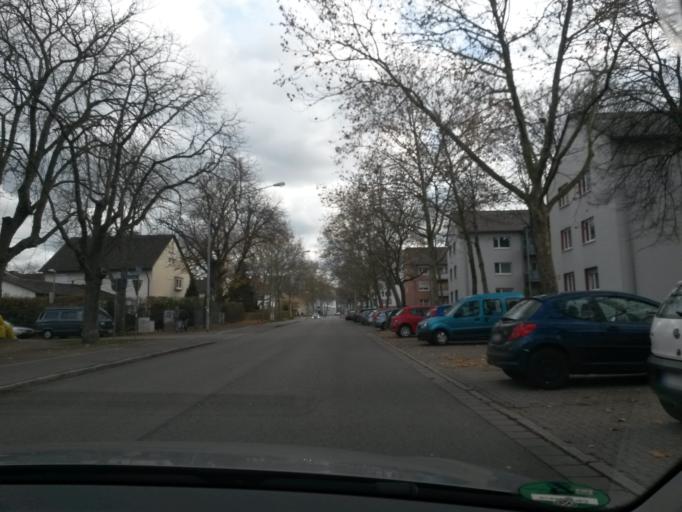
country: DE
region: Baden-Wuerttemberg
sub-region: Freiburg Region
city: Freiburg
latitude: 48.0121
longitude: 7.8282
